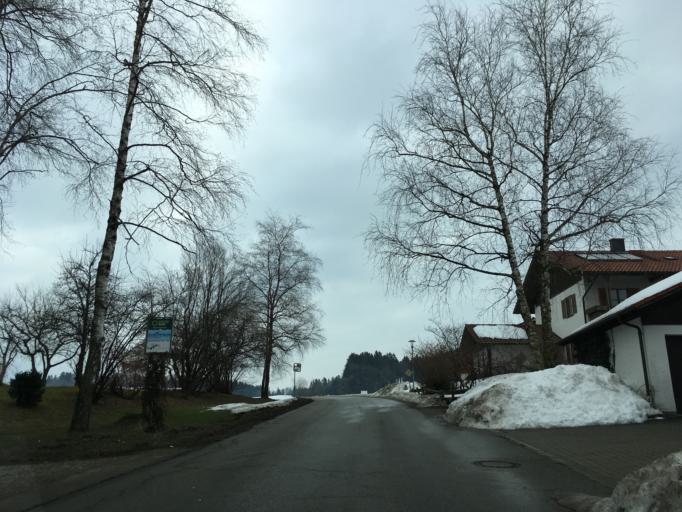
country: DE
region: Bavaria
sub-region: Upper Bavaria
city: Bad Endorf
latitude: 47.9058
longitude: 12.3134
